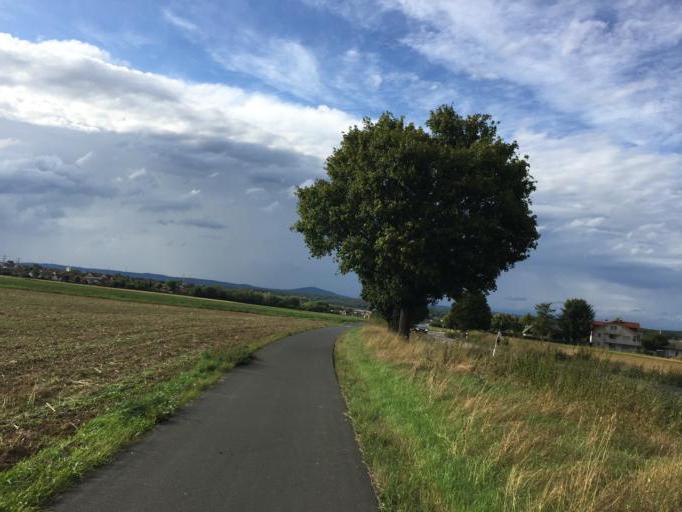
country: DE
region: Hesse
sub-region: Regierungsbezirk Giessen
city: Langgons
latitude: 50.5186
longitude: 8.6758
